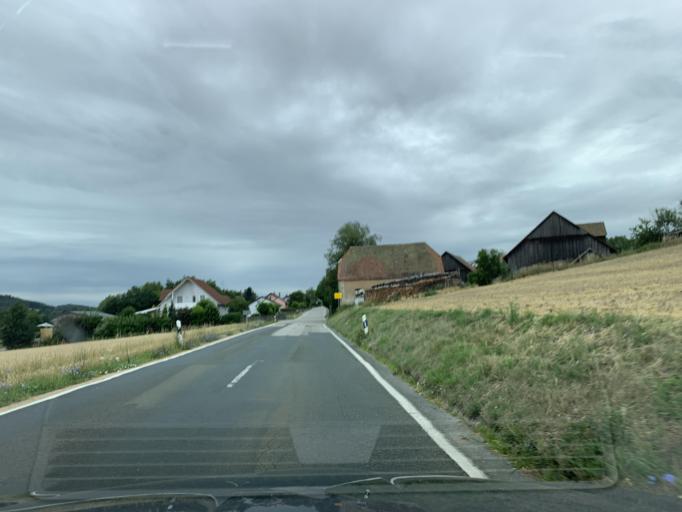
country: DE
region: Bavaria
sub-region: Upper Palatinate
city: Schwarzhofen
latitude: 49.3722
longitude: 12.3482
